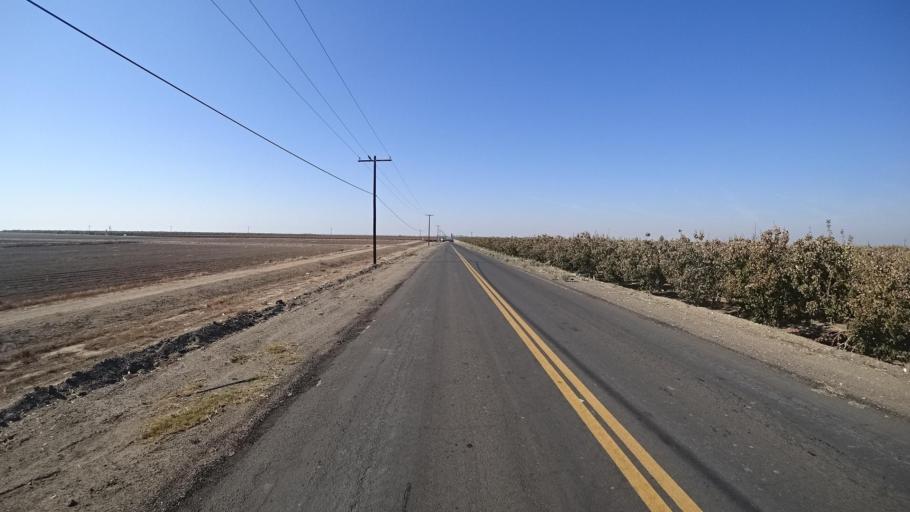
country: US
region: California
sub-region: Kern County
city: McFarland
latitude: 35.7179
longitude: -119.1836
